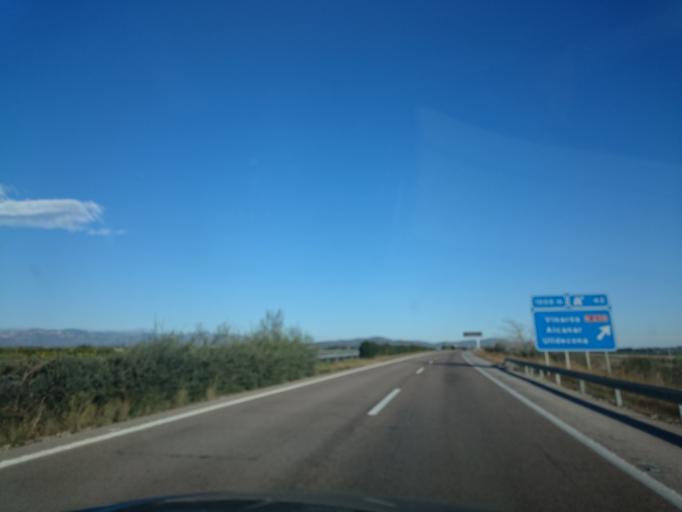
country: ES
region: Catalonia
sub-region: Provincia de Tarragona
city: Ulldecona
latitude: 40.5460
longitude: 0.4199
